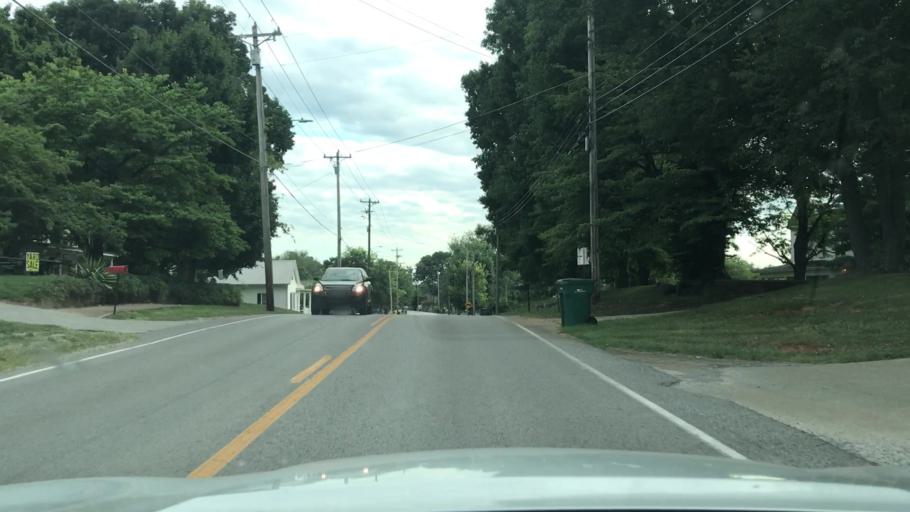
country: US
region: Kentucky
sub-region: Todd County
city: Elkton
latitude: 36.8016
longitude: -87.1572
